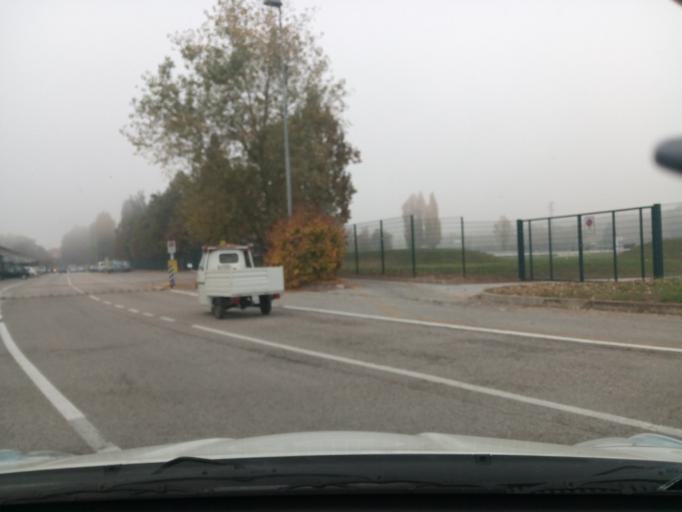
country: IT
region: Veneto
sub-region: Provincia di Vicenza
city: Giavenale
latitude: 45.7119
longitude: 11.3814
